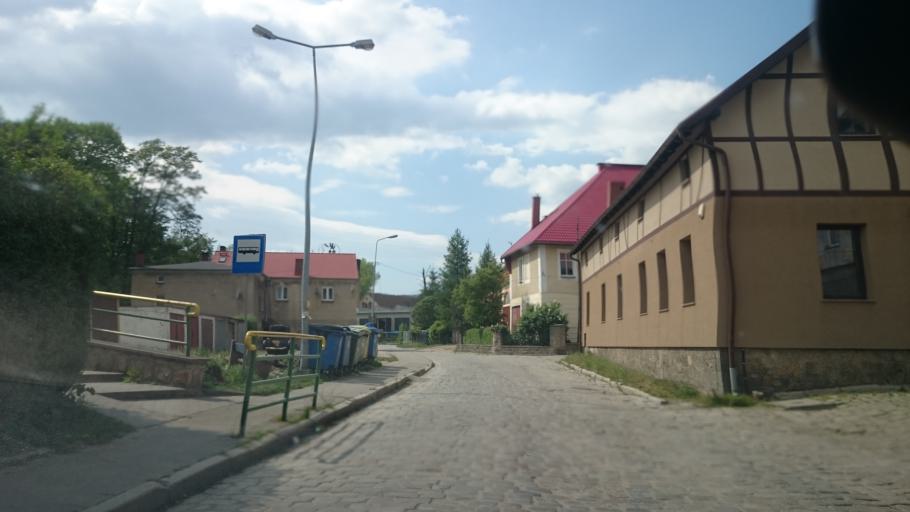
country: PL
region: Lower Silesian Voivodeship
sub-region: Powiat klodzki
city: Bystrzyca Klodzka
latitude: 50.2965
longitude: 16.6491
